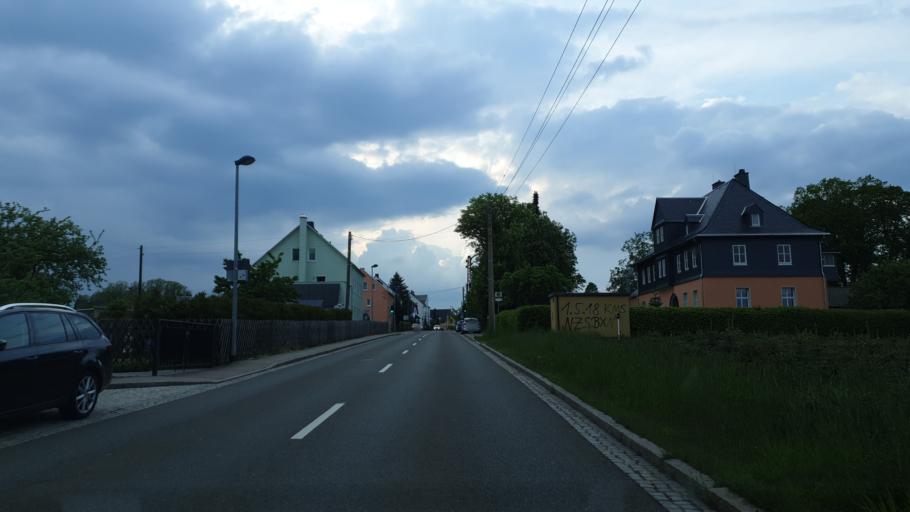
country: DE
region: Saxony
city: Lugau
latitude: 50.7091
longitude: 12.7342
